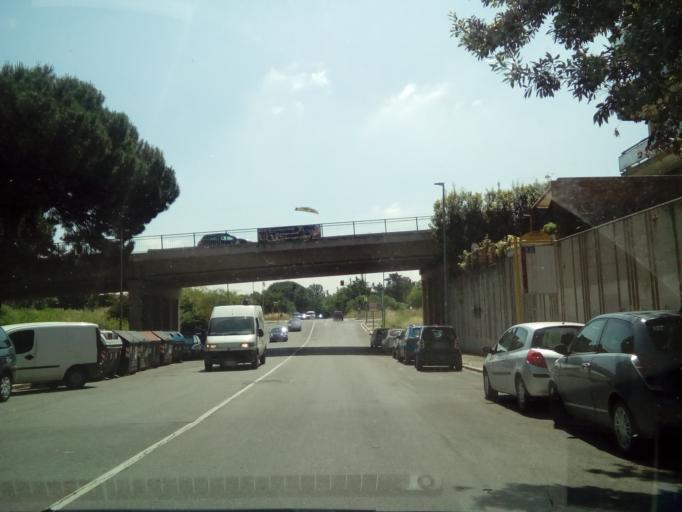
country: IT
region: Latium
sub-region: Citta metropolitana di Roma Capitale
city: Rome
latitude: 41.8820
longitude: 12.5904
